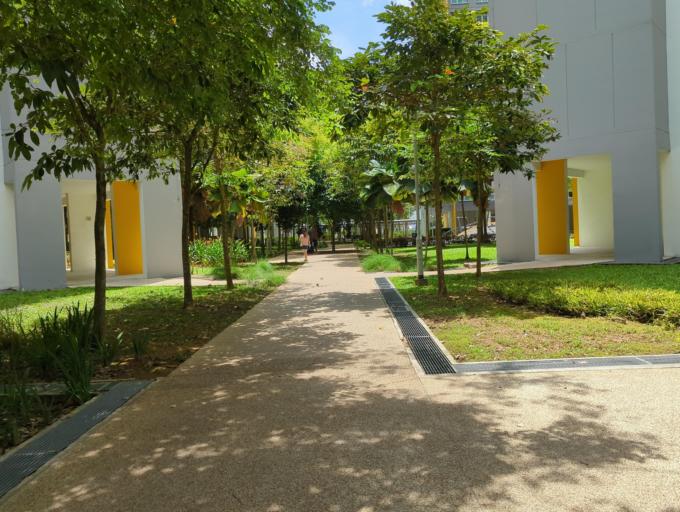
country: MY
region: Johor
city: Kampung Pasir Gudang Baru
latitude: 1.3899
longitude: 103.8937
